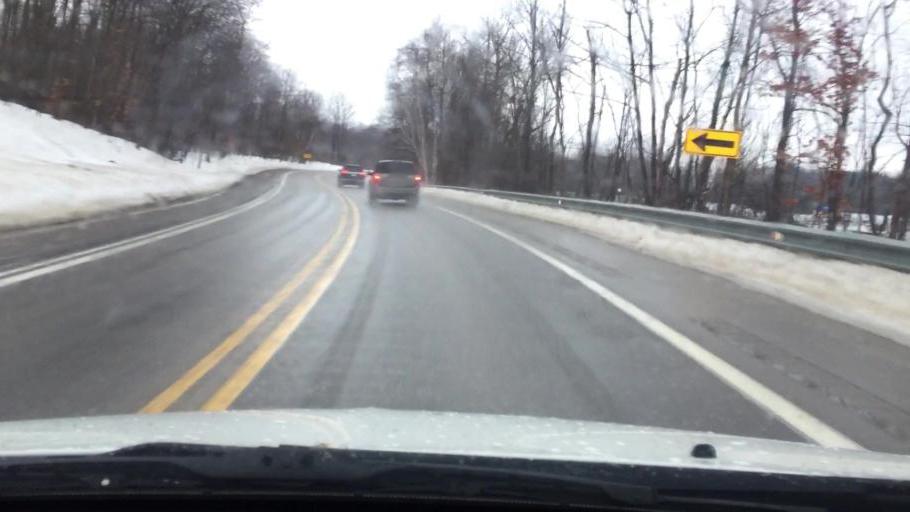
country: US
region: Michigan
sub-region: Charlevoix County
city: East Jordan
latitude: 45.2094
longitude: -85.1686
